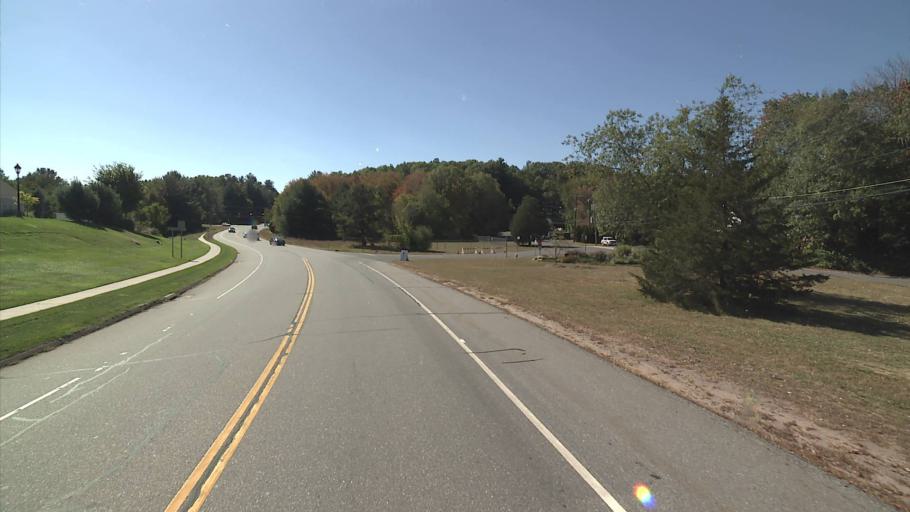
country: US
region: Connecticut
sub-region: Hartford County
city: Manchester
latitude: 41.7141
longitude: -72.5266
